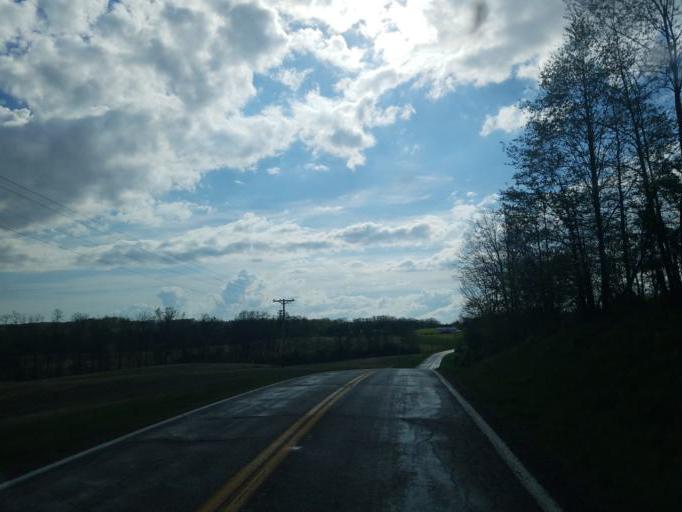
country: US
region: Ohio
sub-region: Knox County
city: Oak Hill
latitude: 40.3850
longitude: -82.2428
